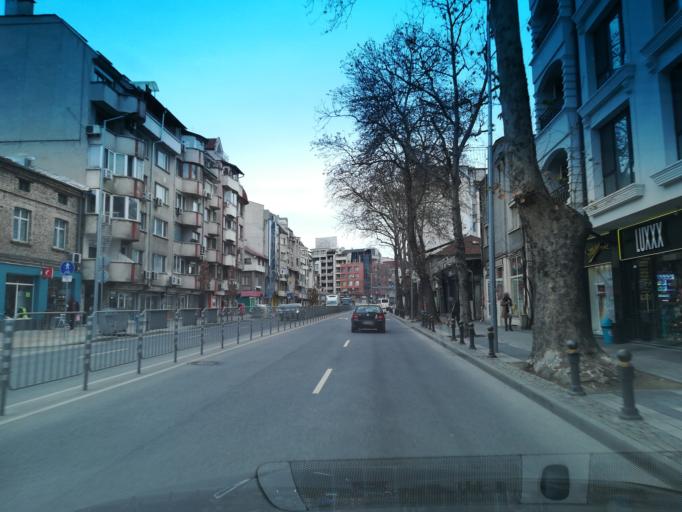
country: BG
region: Plovdiv
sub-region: Obshtina Plovdiv
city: Plovdiv
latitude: 42.1406
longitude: 24.7354
